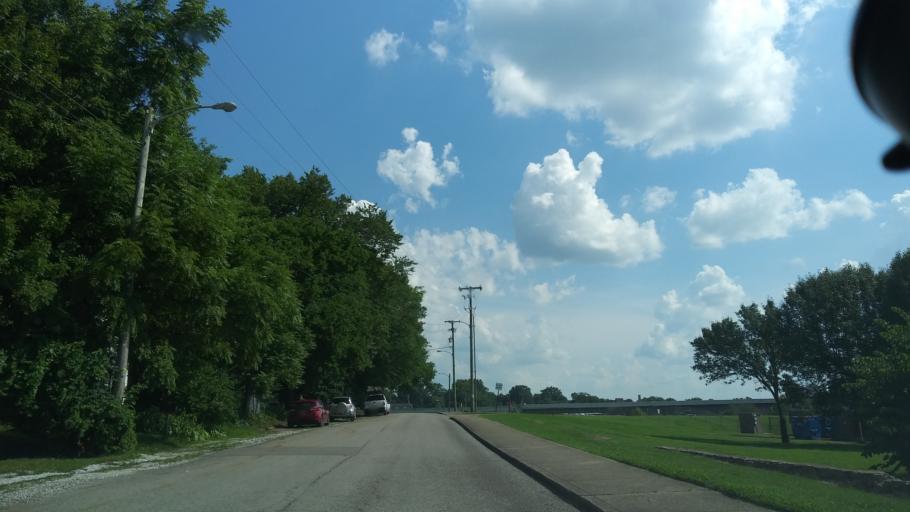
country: US
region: Tennessee
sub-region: Davidson County
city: Nashville
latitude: 36.1565
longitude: -86.8438
